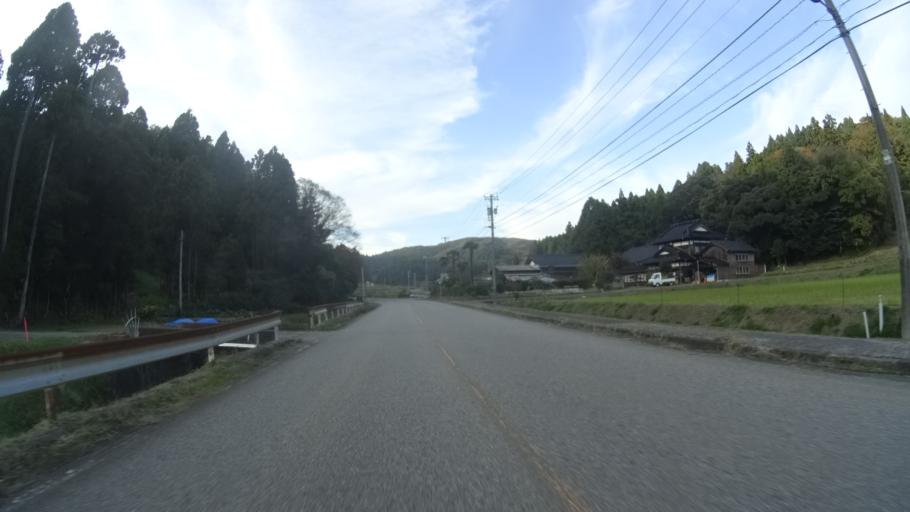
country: JP
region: Ishikawa
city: Nanao
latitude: 37.1932
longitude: 136.7166
